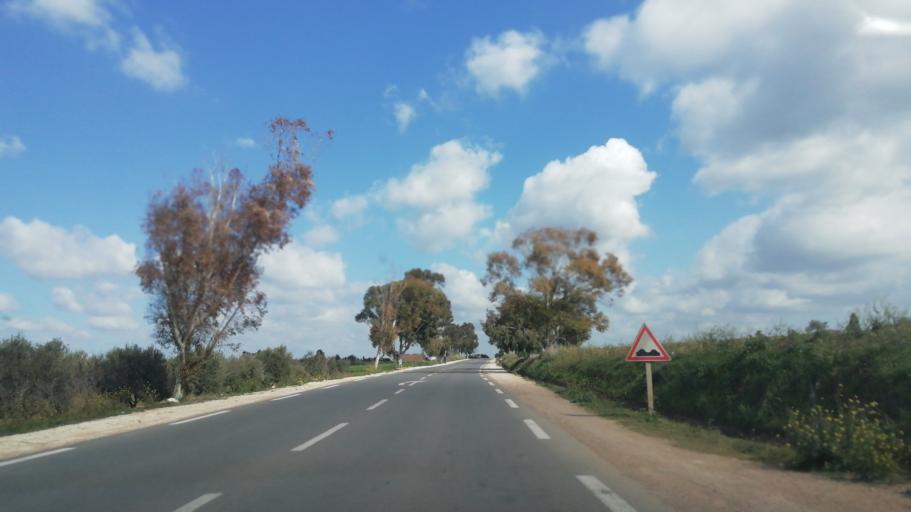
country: DZ
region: Relizane
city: Relizane
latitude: 35.7156
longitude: 0.2993
